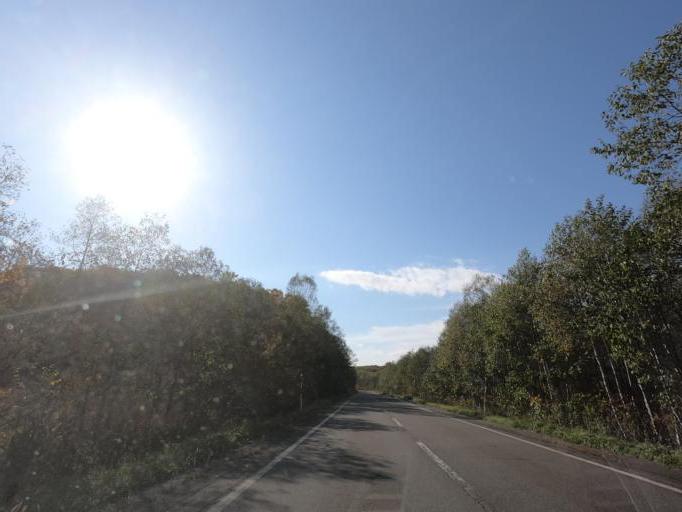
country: JP
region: Hokkaido
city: Obihiro
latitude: 42.6385
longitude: 143.4923
